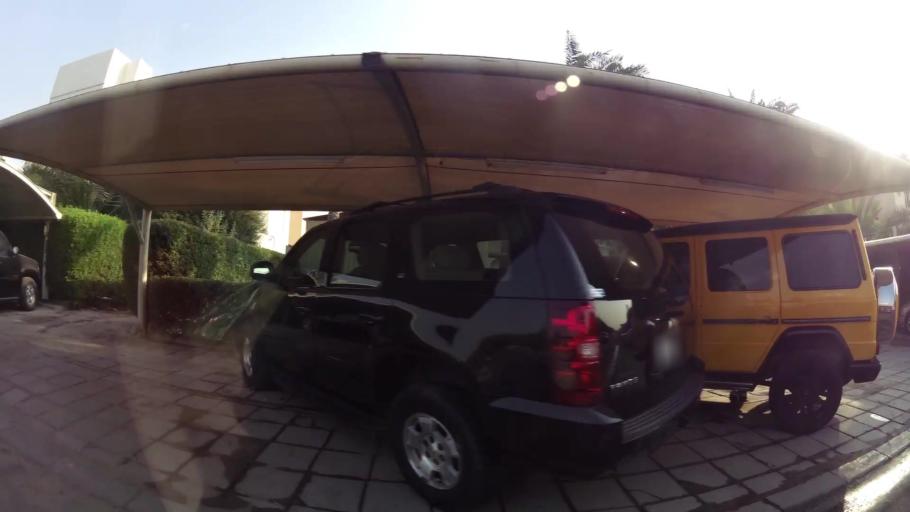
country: KW
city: Bayan
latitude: 29.3035
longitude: 48.0466
